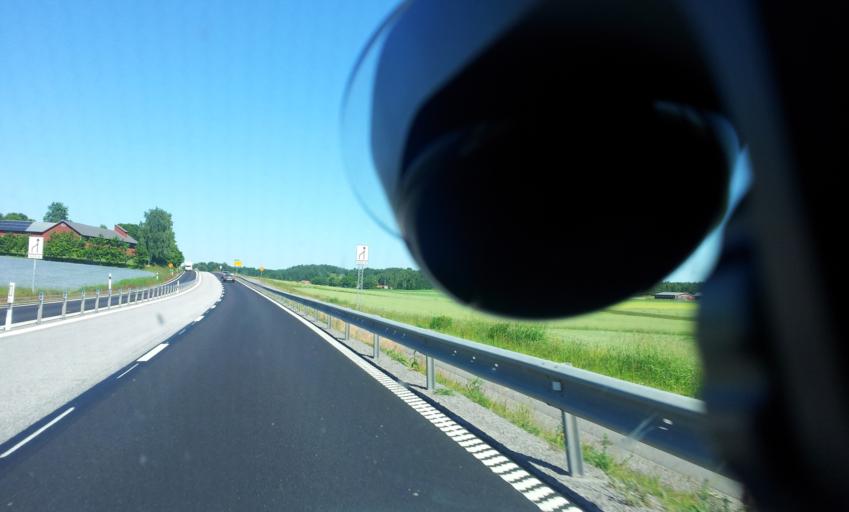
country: SE
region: OEstergoetland
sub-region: Soderkopings Kommun
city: Soederkoeping
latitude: 58.5377
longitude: 16.2801
